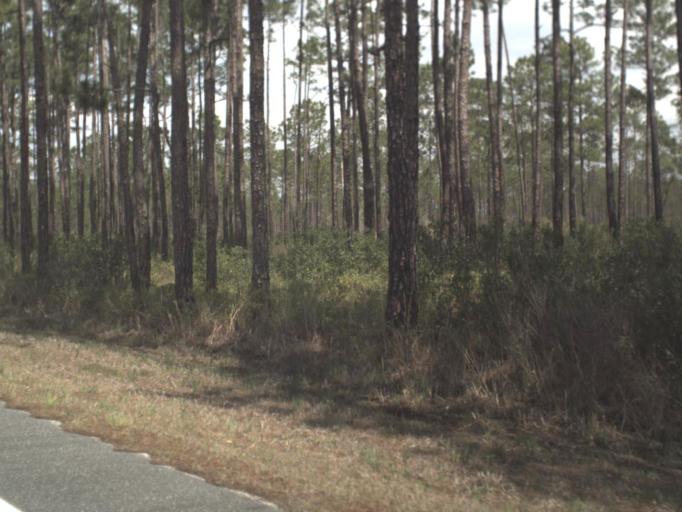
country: US
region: Florida
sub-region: Franklin County
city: Apalachicola
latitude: 29.9430
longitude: -84.9766
